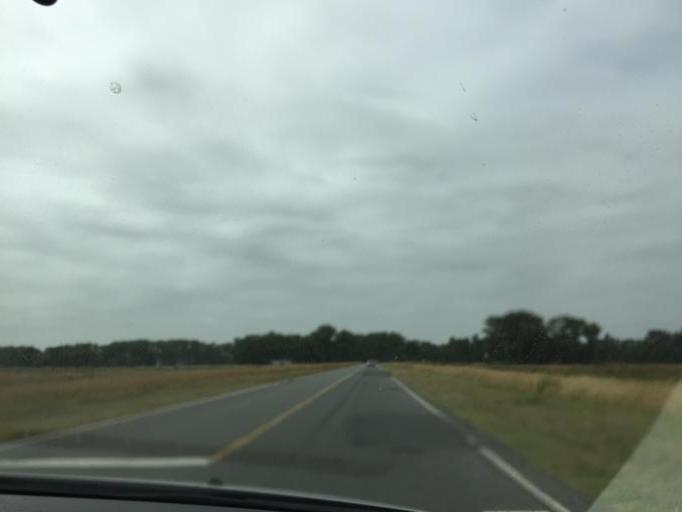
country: AR
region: Buenos Aires
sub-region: Partido de Las Flores
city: Las Flores
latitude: -36.2122
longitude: -59.0464
